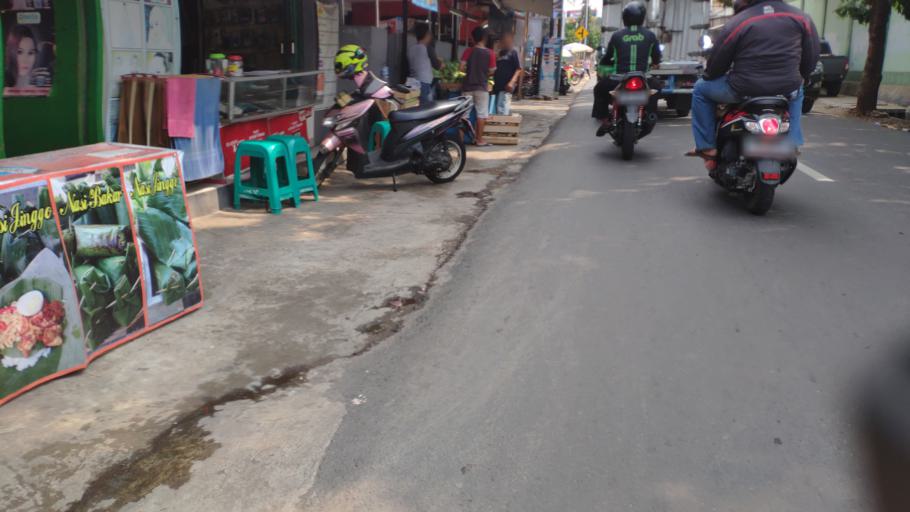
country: ID
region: West Java
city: Depok
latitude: -6.3131
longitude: 106.8256
